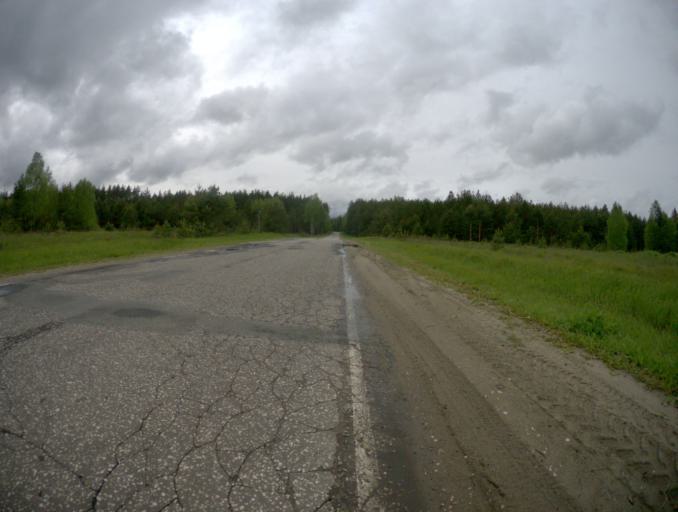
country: RU
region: Vladimir
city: Velikodvorskiy
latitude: 55.3927
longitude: 40.7266
